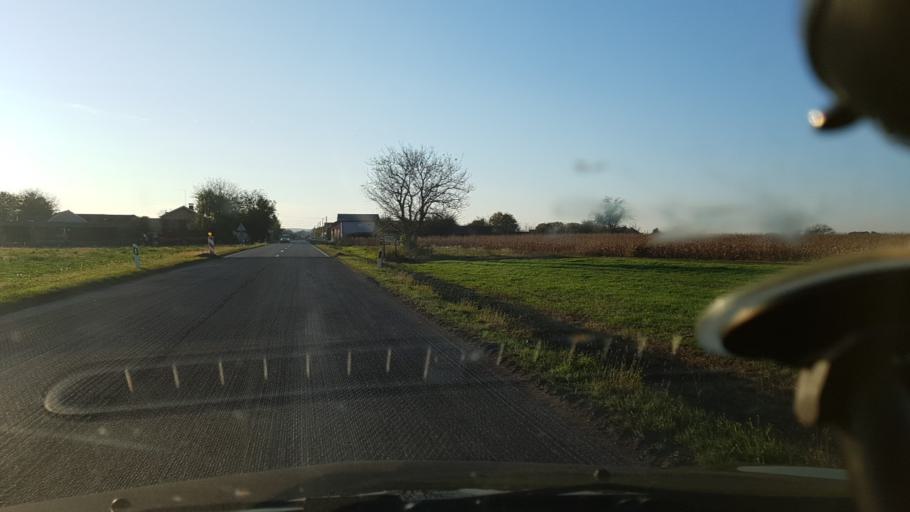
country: HR
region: Koprivnicko-Krizevacka
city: Virje
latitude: 46.0590
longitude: 17.0134
